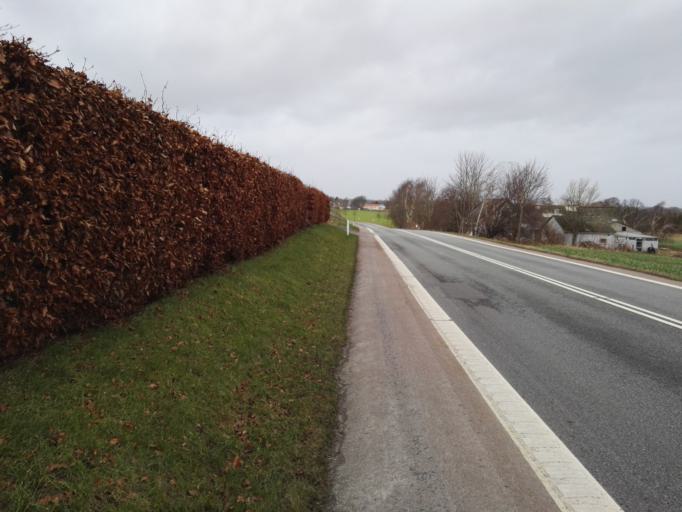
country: DK
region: Capital Region
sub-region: Frederikssund Kommune
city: Skibby
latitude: 55.6793
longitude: 11.9277
